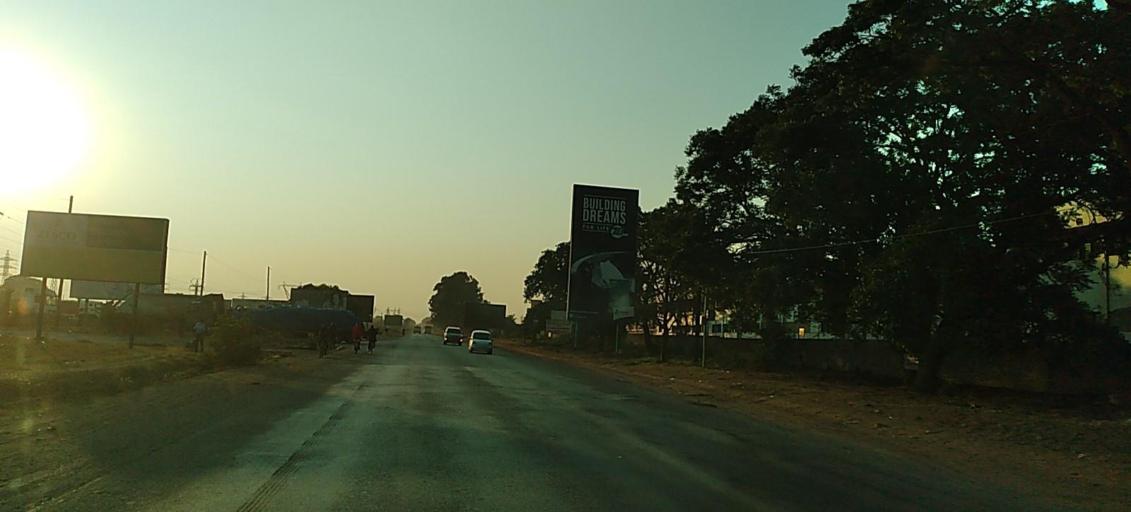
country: ZM
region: Copperbelt
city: Ndola
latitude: -13.0172
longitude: 28.6650
